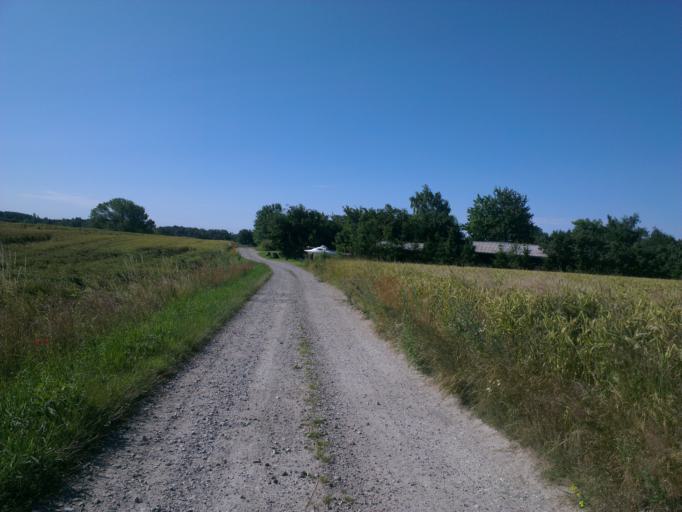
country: DK
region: Capital Region
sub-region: Frederikssund Kommune
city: Frederikssund
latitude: 55.7960
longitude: 12.0313
